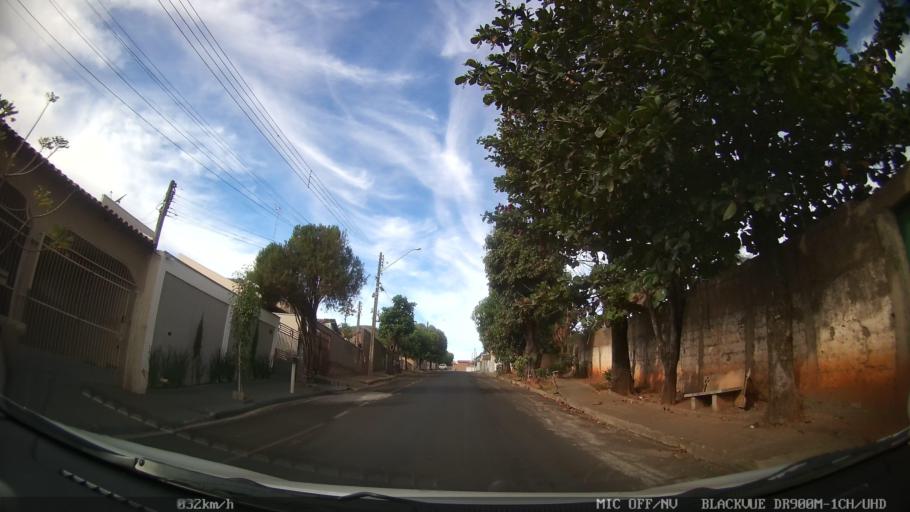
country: BR
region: Sao Paulo
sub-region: Catanduva
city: Catanduva
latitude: -21.1364
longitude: -48.9935
